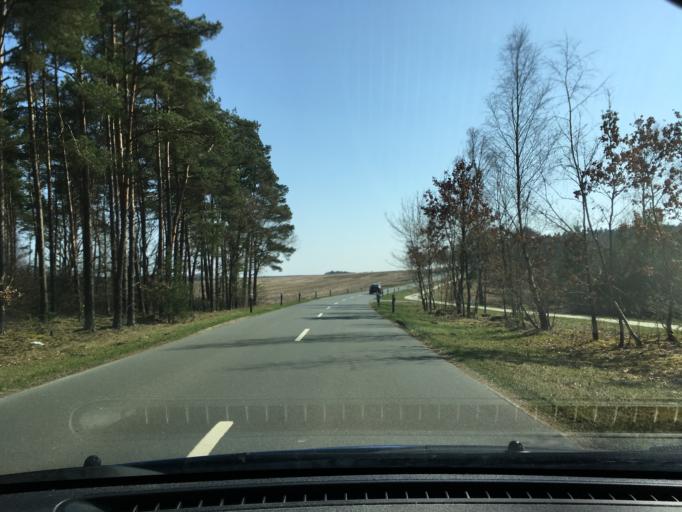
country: DE
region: Lower Saxony
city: Eimke
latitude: 52.9898
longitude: 10.3061
